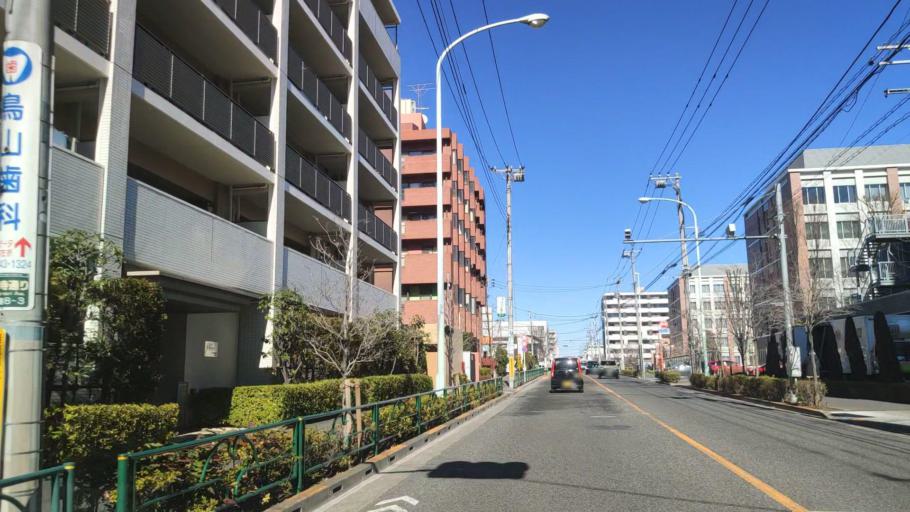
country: JP
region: Tokyo
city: Mitaka-shi
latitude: 35.6841
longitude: 139.5684
